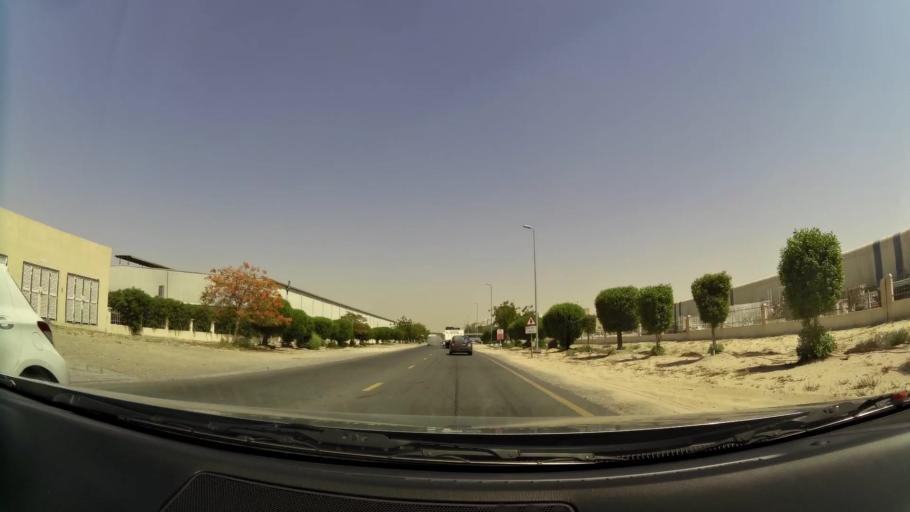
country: AE
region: Dubai
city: Dubai
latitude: 24.9843
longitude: 55.1577
